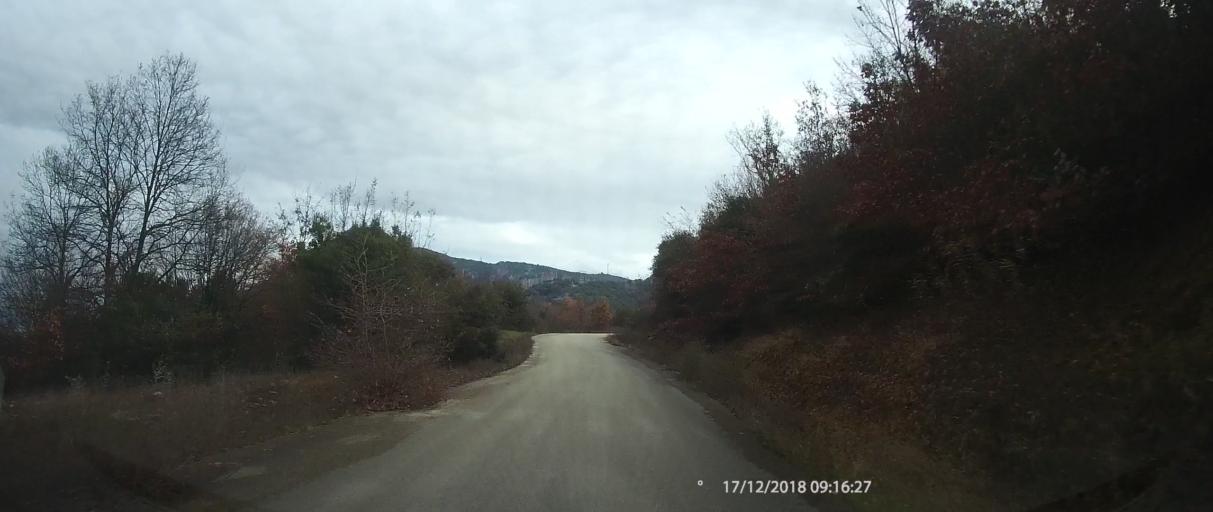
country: GR
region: Epirus
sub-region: Nomos Ioanninon
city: Kalpaki
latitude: 39.9608
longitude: 20.6575
